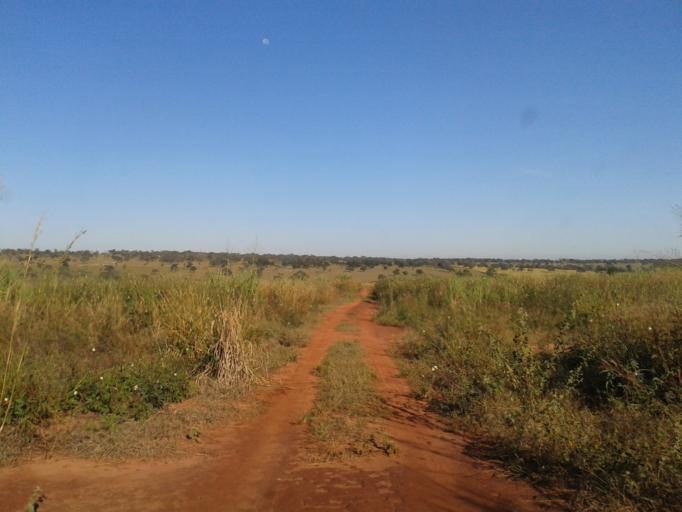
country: BR
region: Minas Gerais
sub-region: Santa Vitoria
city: Santa Vitoria
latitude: -19.0195
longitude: -50.3738
